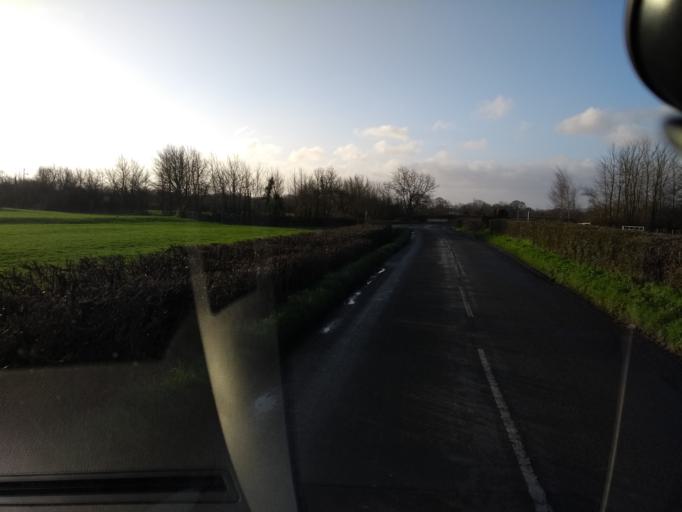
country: GB
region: England
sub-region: Somerset
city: Bridgwater
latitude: 51.1466
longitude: -3.0045
